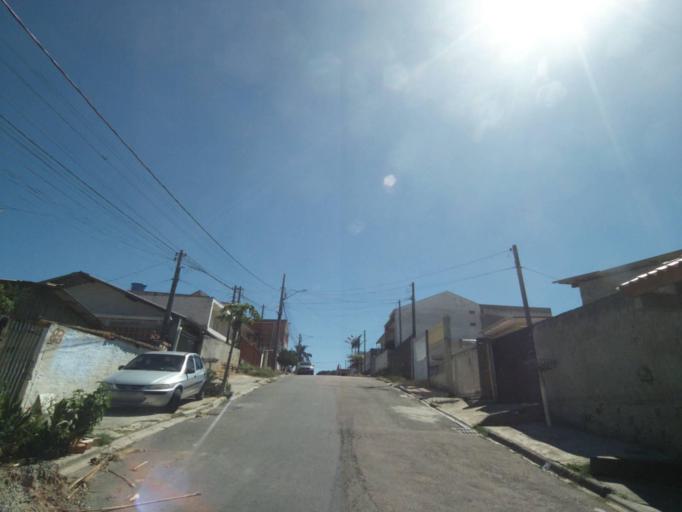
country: BR
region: Parana
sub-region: Curitiba
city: Curitiba
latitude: -25.4625
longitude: -49.3405
